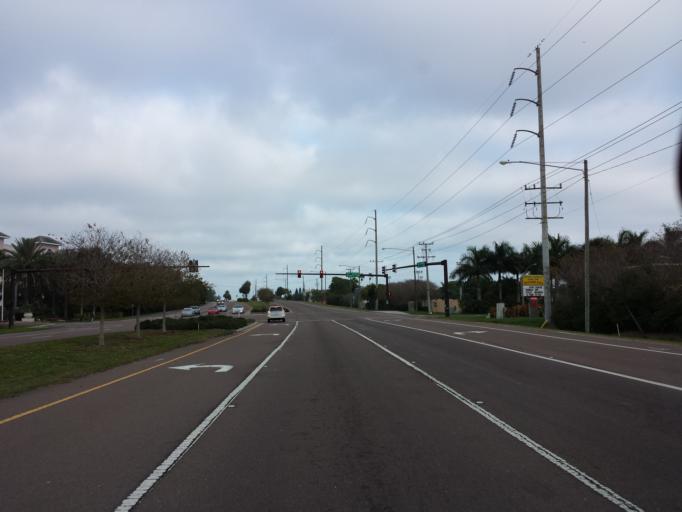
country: US
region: Florida
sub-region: Pinellas County
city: Gulfport
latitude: 27.7164
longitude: -82.7020
